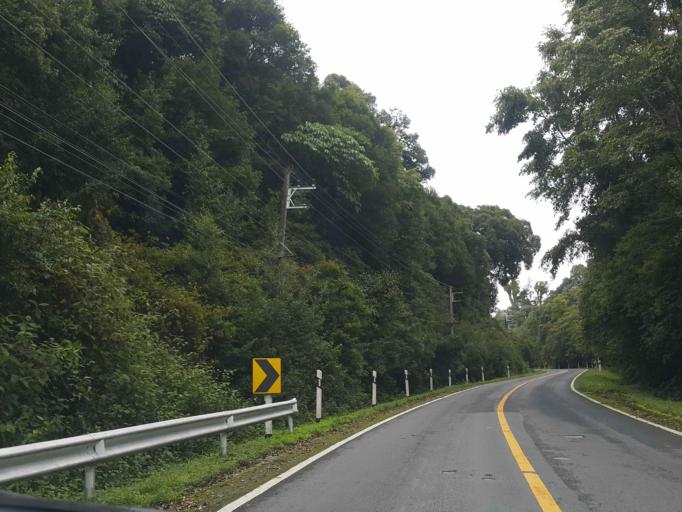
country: TH
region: Chiang Mai
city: Mae Chaem
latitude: 18.5760
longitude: 98.4824
